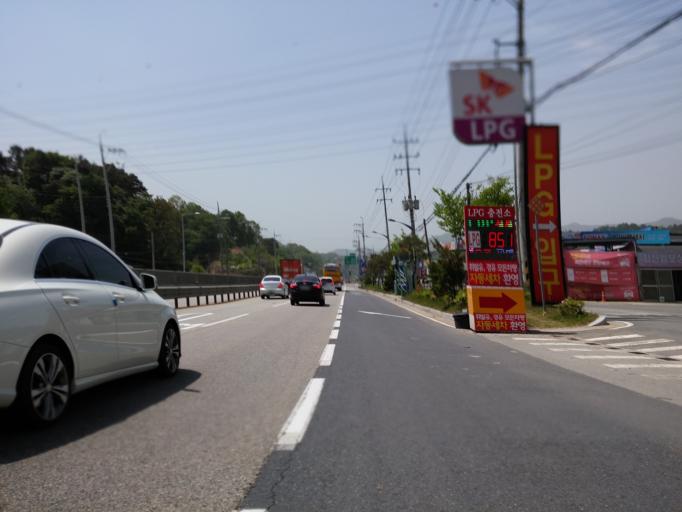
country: KR
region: Chungcheongnam-do
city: Nonsan
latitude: 36.2758
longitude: 127.2363
